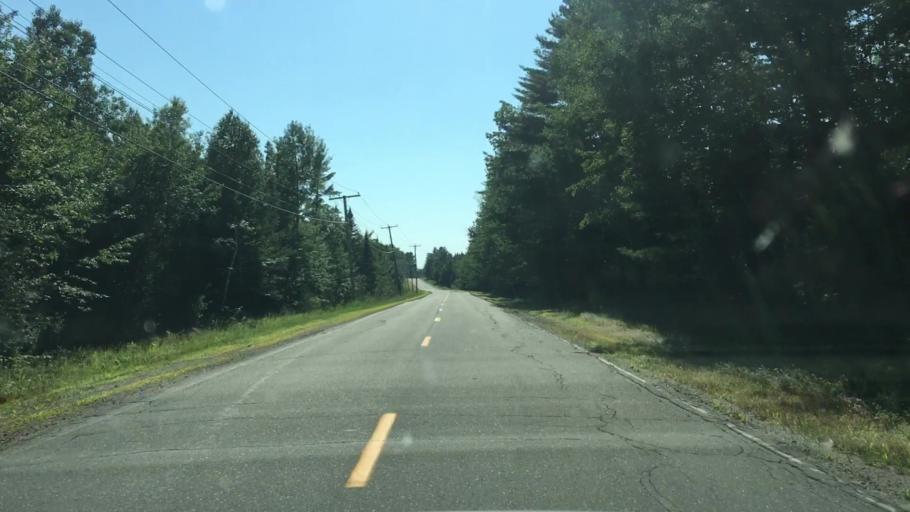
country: US
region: Maine
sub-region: Penobscot County
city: Enfield
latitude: 45.2447
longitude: -68.6102
